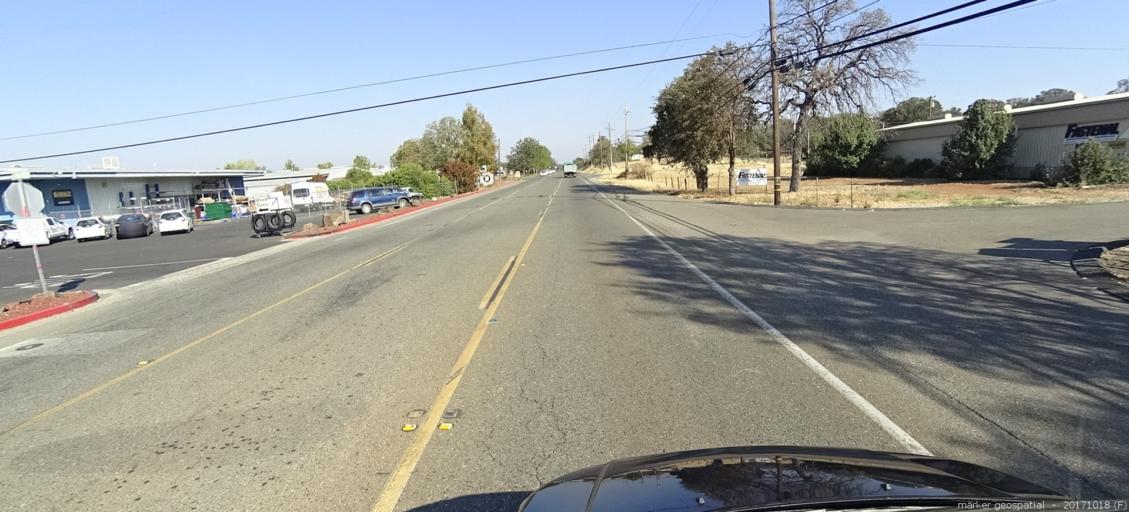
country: US
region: California
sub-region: Shasta County
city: Palo Cedro
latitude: 40.5459
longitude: -122.3028
